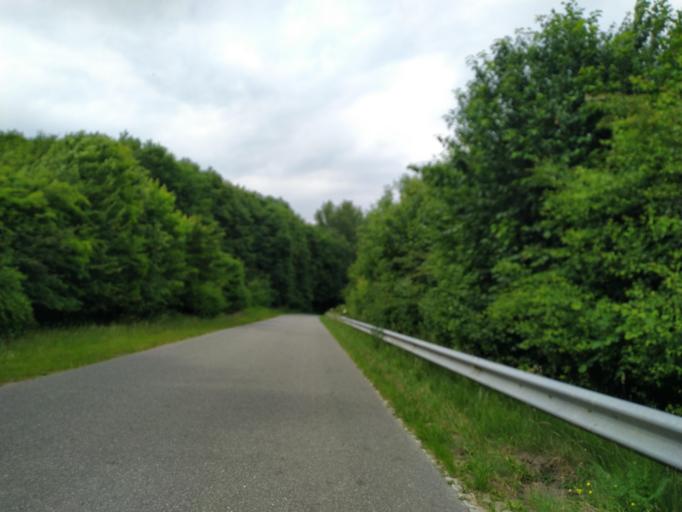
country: DE
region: Schleswig-Holstein
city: Gross Gronau
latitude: 53.7925
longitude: 10.7263
